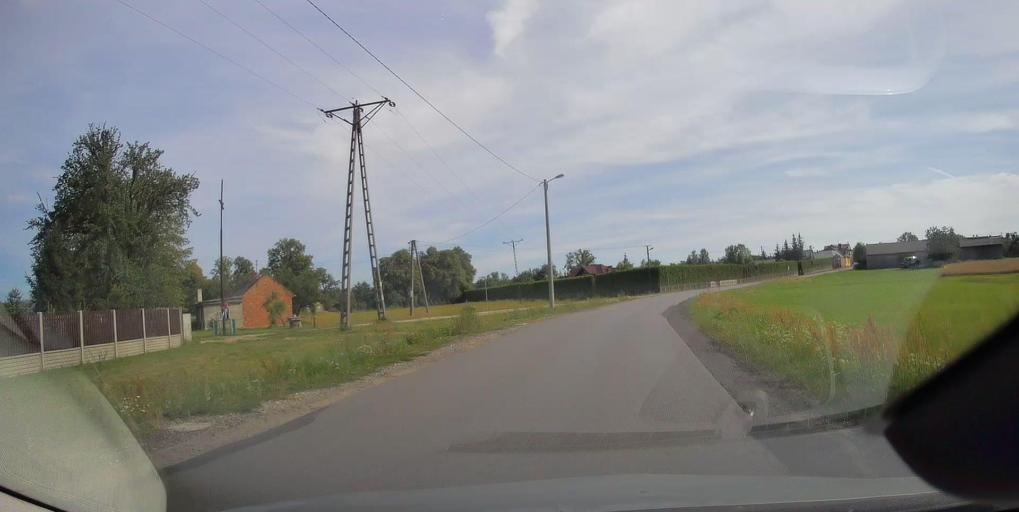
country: PL
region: Lodz Voivodeship
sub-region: Powiat tomaszowski
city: Tomaszow Mazowiecki
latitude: 51.4570
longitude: 20.0359
